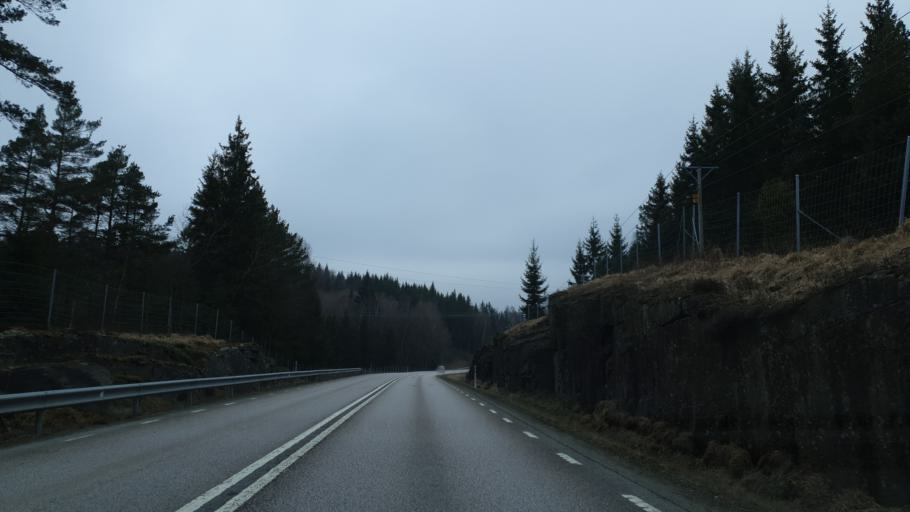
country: SE
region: Vaestra Goetaland
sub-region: Harryda Kommun
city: Hindas
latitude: 57.6385
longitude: 12.4069
